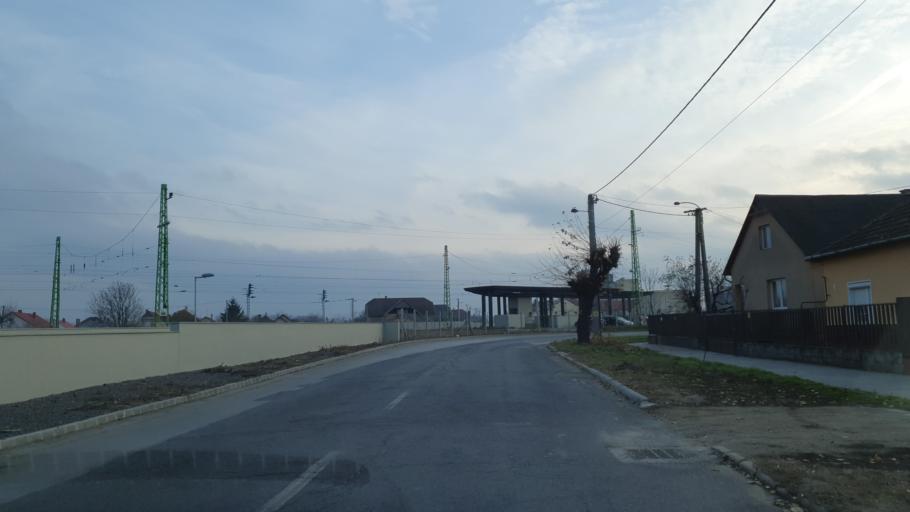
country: HU
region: Szabolcs-Szatmar-Bereg
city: Kisvarda
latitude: 48.2108
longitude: 22.0802
